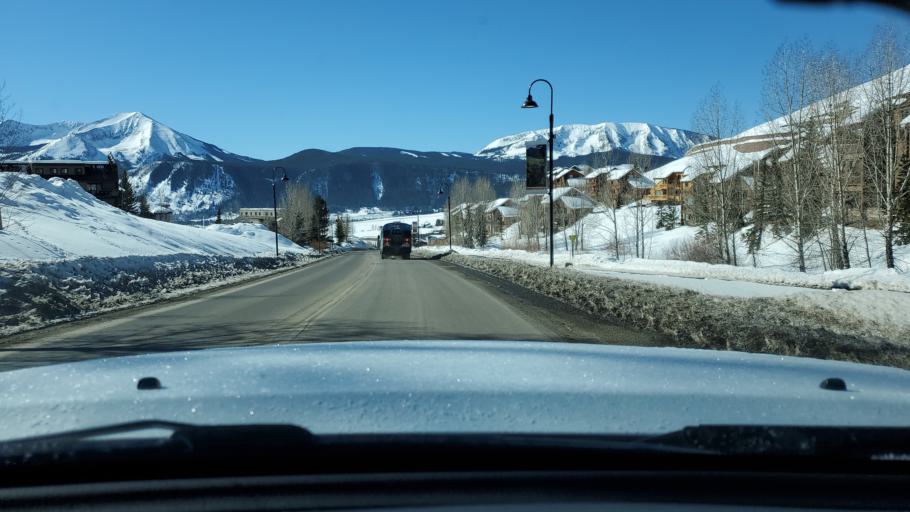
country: US
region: Colorado
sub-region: Gunnison County
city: Crested Butte
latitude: 38.8981
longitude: -106.9678
